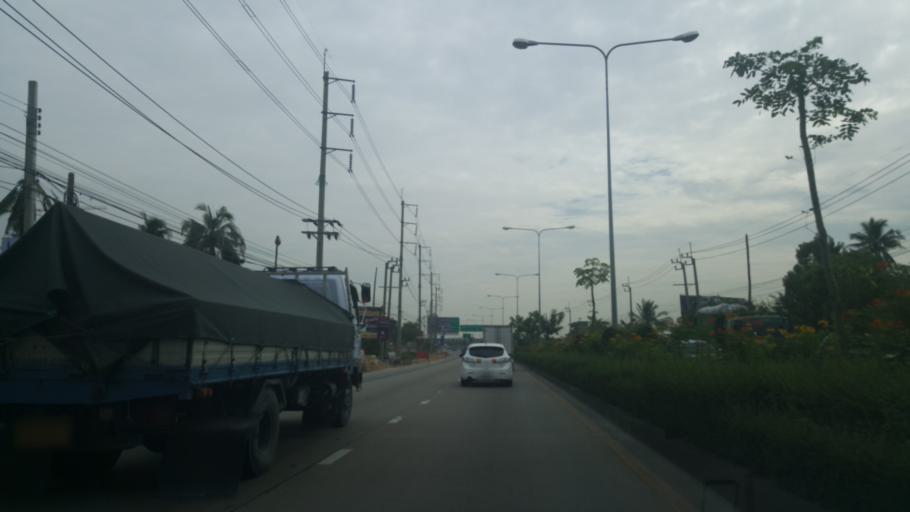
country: TH
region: Bangkok
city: Bang Khae
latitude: 13.6834
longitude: 100.4174
